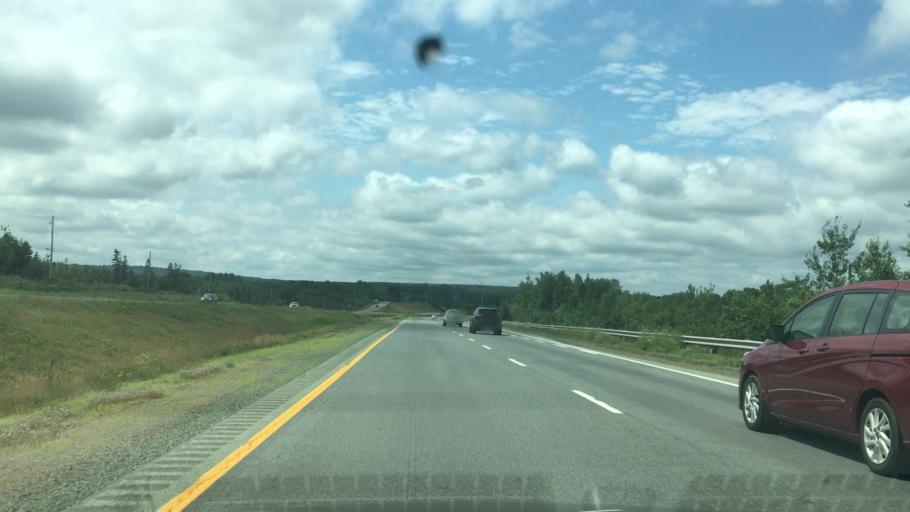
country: CA
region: Nova Scotia
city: Springhill
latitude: 45.6953
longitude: -63.9951
